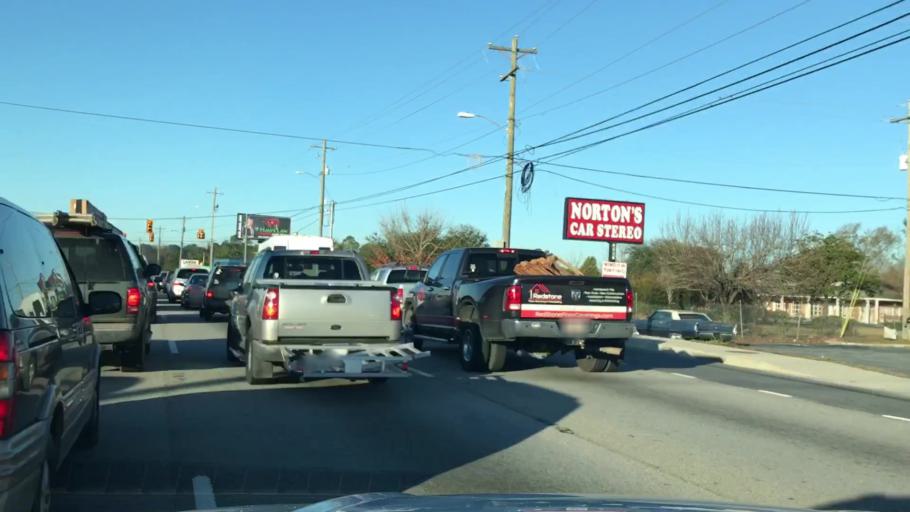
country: US
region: South Carolina
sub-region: Berkeley County
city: Hanahan
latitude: 32.9298
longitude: -80.0716
